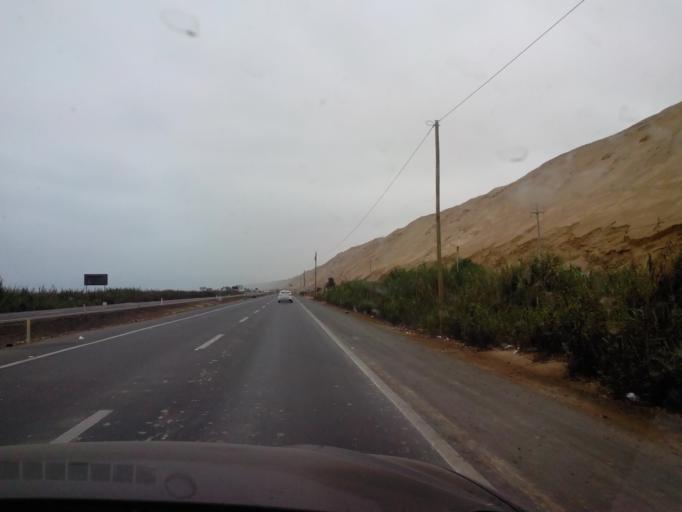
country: PE
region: Ica
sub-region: Provincia de Chincha
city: San Pedro
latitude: -13.4003
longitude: -76.1952
